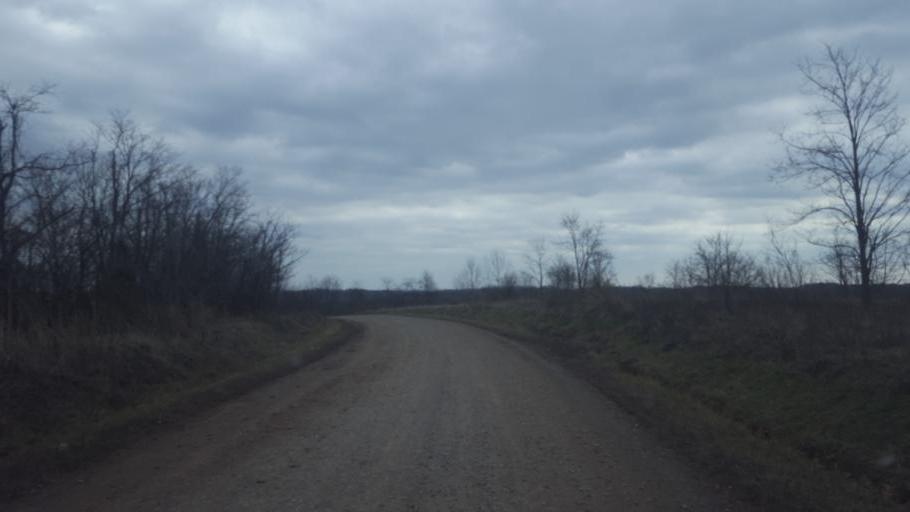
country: US
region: Ohio
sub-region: Gallia County
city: Gallipolis
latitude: 38.7360
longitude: -82.3278
